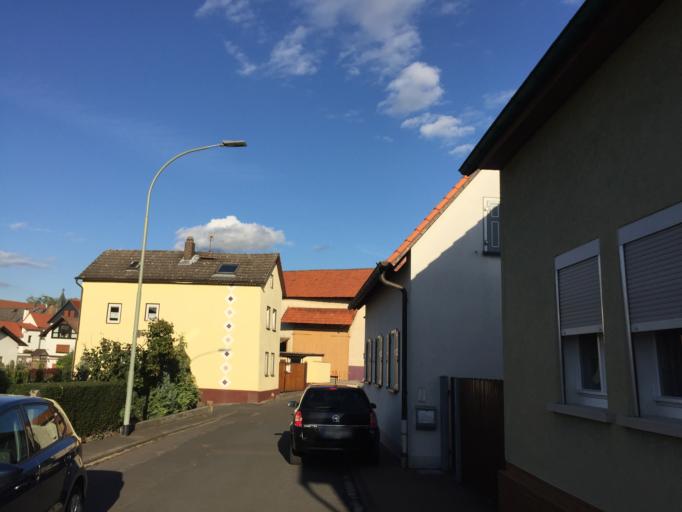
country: DE
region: Hesse
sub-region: Regierungsbezirk Darmstadt
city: Munzenberg
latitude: 50.4536
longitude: 8.7748
